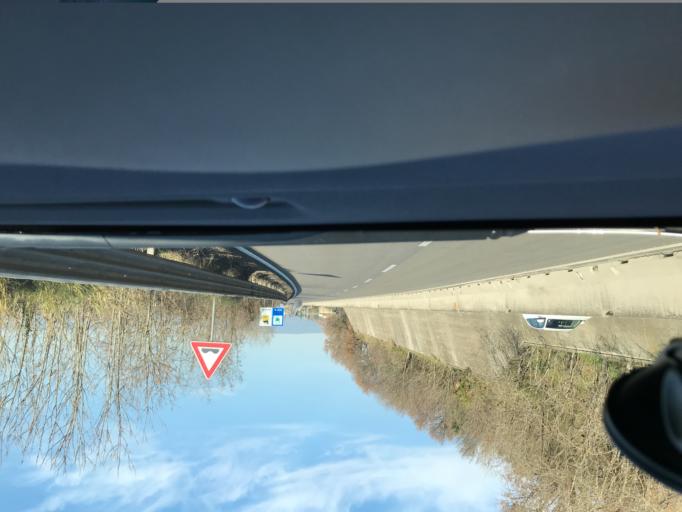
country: IT
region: Latium
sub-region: Provincia di Viterbo
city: Orte Scalo
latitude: 42.4560
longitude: 12.4121
